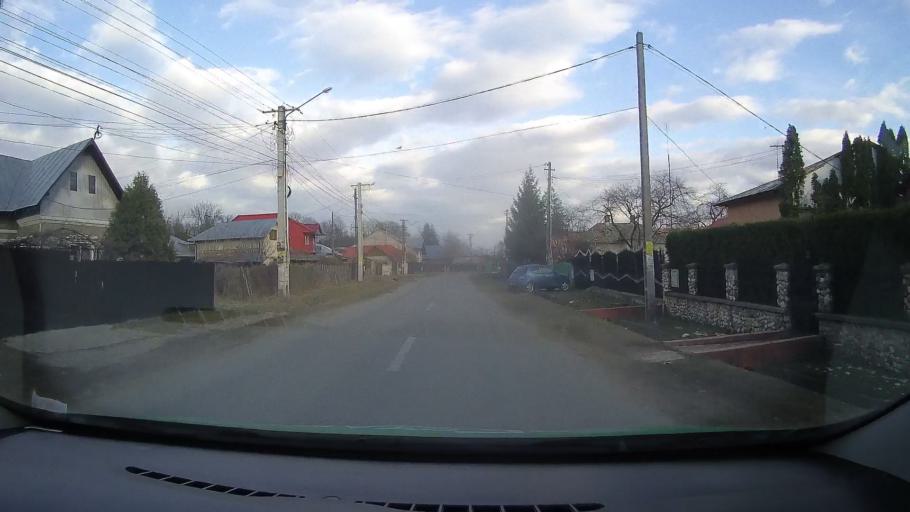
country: RO
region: Dambovita
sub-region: Comuna Gura Ocnitei
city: Gura Ocnitei
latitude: 44.9395
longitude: 25.5704
